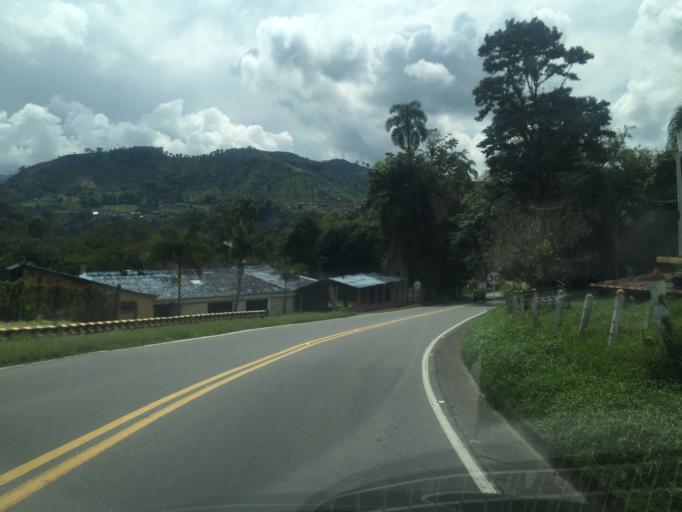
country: CO
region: Caldas
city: Chinchina
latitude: 4.9939
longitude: -75.6018
